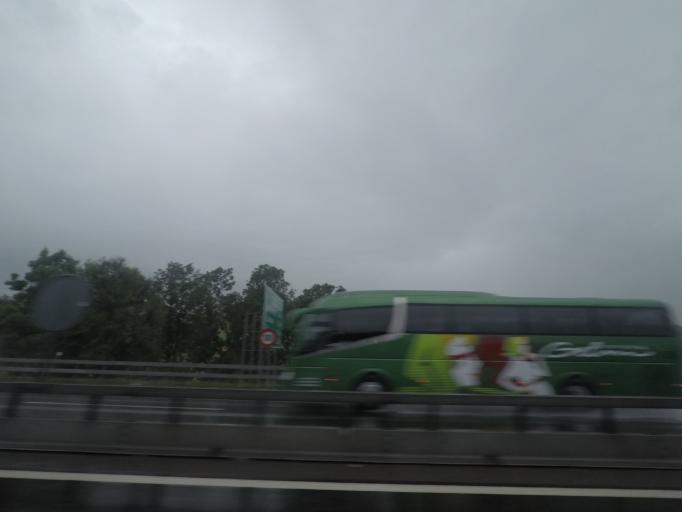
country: CH
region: Fribourg
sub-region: Gruyere District
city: Vuadens
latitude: 46.6234
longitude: 7.0291
